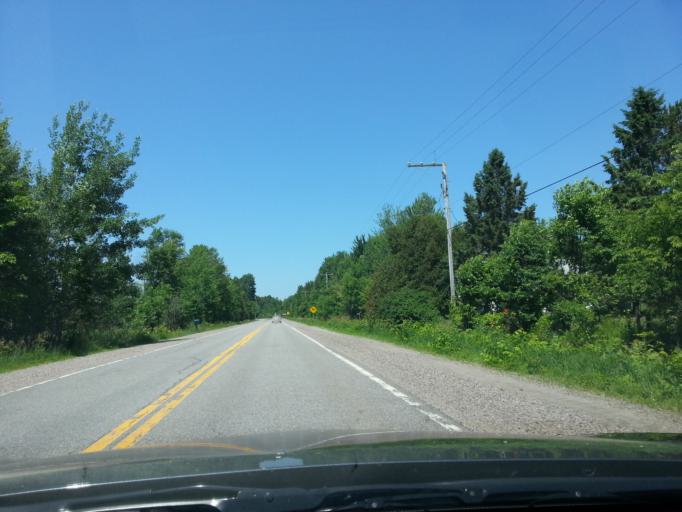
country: CA
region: Ontario
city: Arnprior
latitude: 45.5480
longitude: -76.3514
